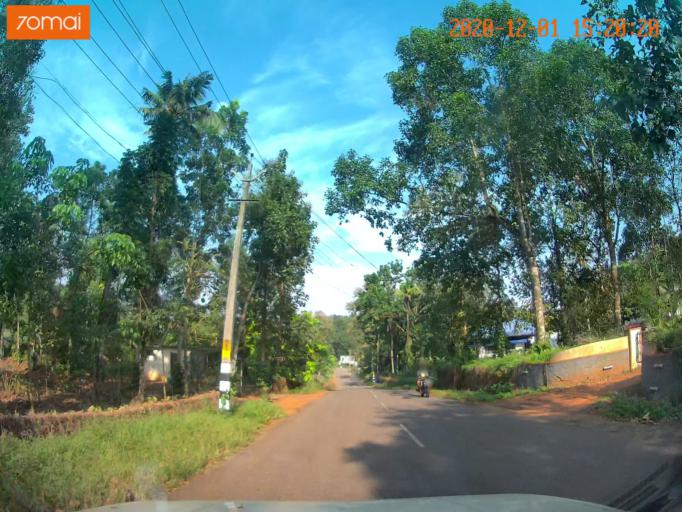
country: IN
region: Kerala
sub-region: Ernakulam
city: Ramamangalam
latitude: 9.9423
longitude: 76.5386
